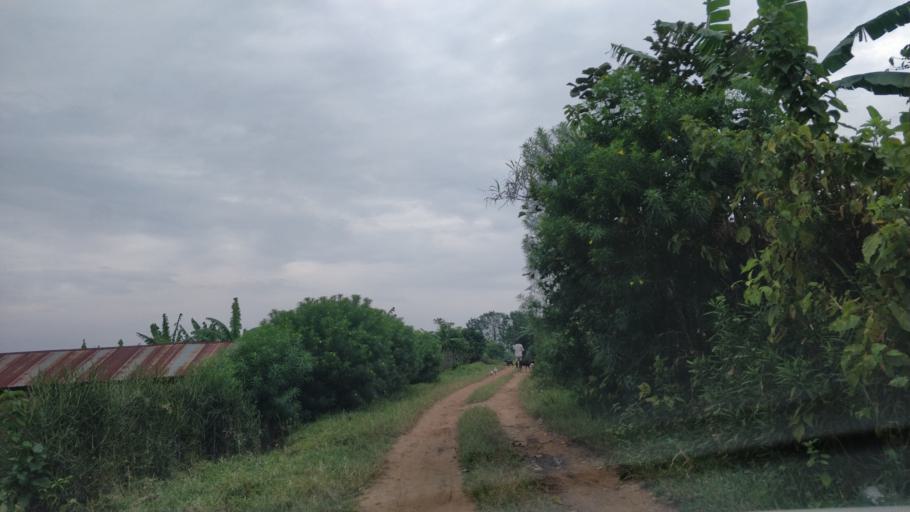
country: UG
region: Western Region
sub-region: Sheema District
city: Kibingo
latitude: -0.6998
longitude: 30.3922
